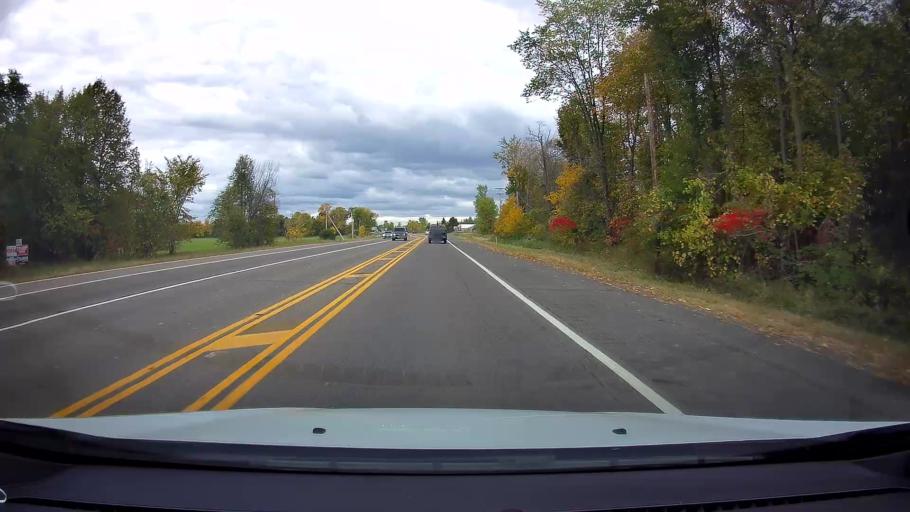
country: US
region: Minnesota
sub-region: Chisago County
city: Chisago City
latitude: 45.3560
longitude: -92.9103
